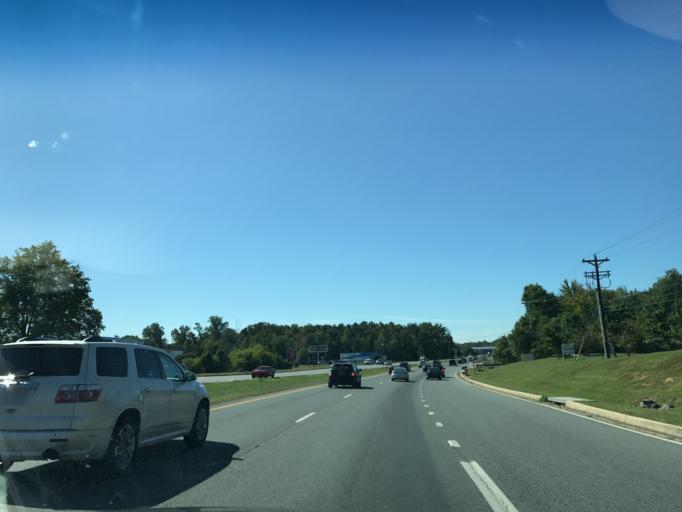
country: US
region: Maryland
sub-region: Charles County
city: Saint Charles
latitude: 38.5964
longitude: -76.9381
